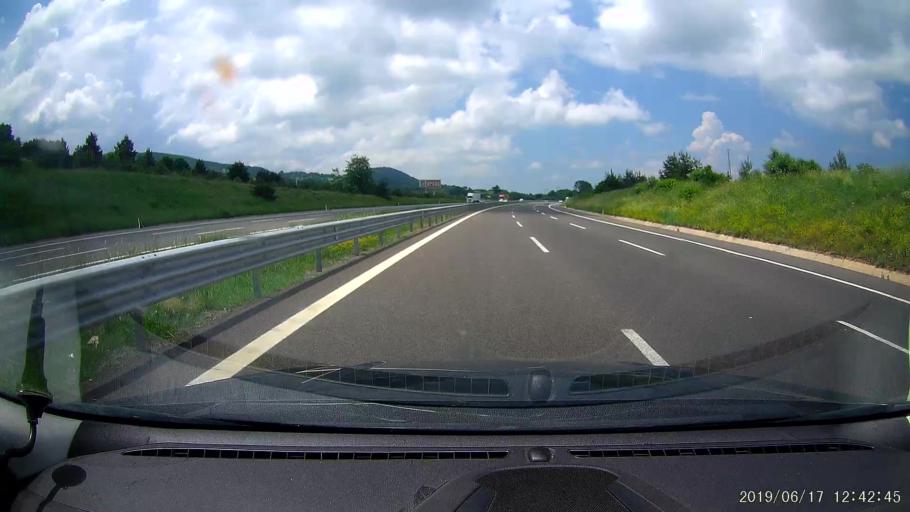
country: TR
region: Bolu
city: Yenicaga
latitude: 40.7513
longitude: 31.9376
